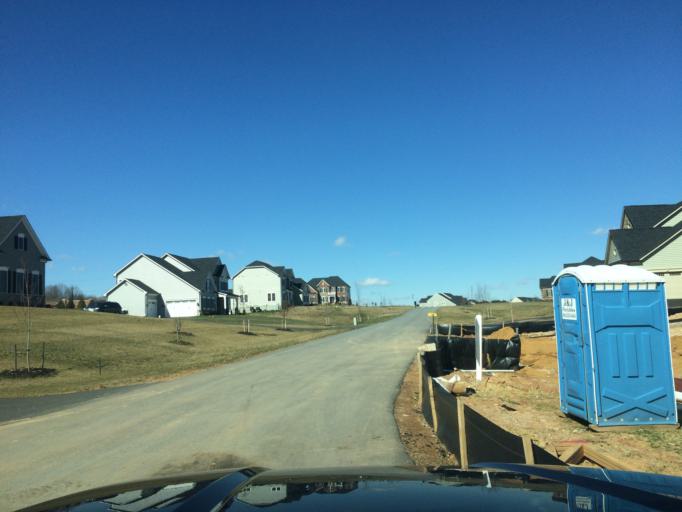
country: US
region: Maryland
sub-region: Carroll County
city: Eldersburg
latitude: 39.4368
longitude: -76.9724
